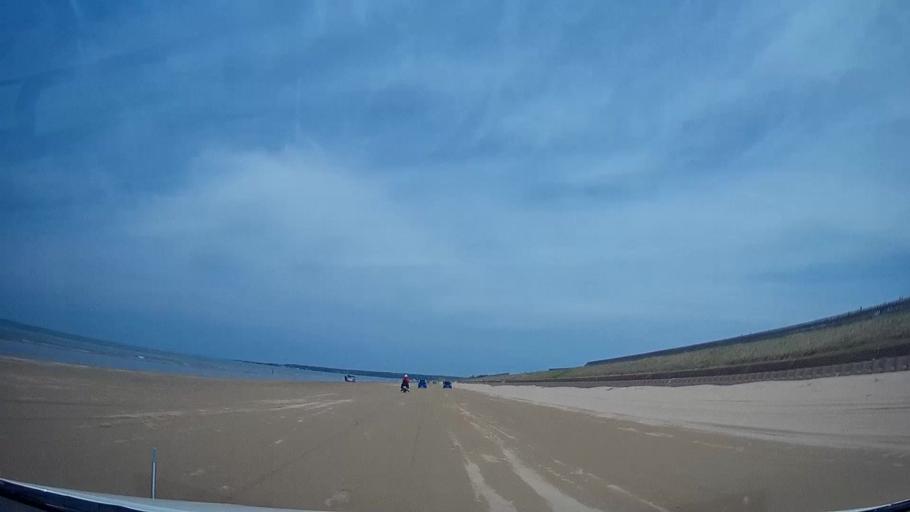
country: JP
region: Ishikawa
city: Hakui
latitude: 36.8765
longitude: 136.7614
